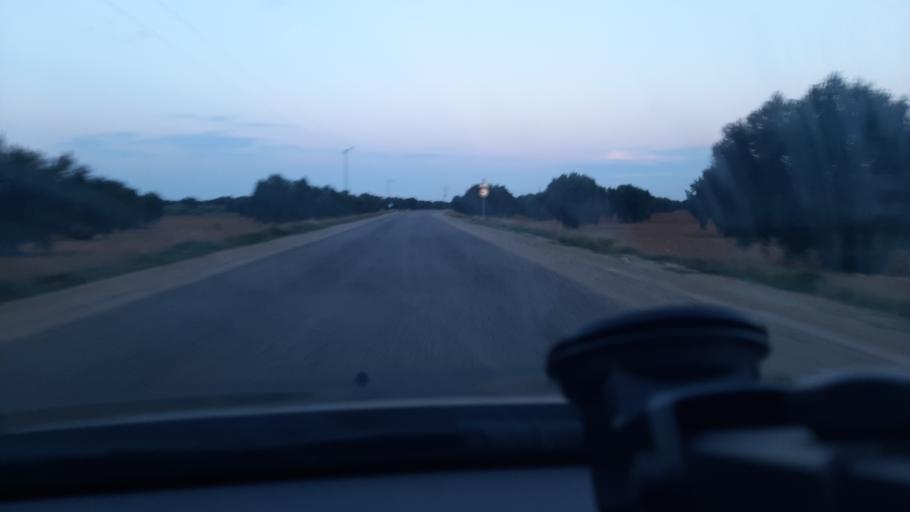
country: TN
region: Al Mahdiyah
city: Shurban
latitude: 35.0126
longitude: 10.4315
